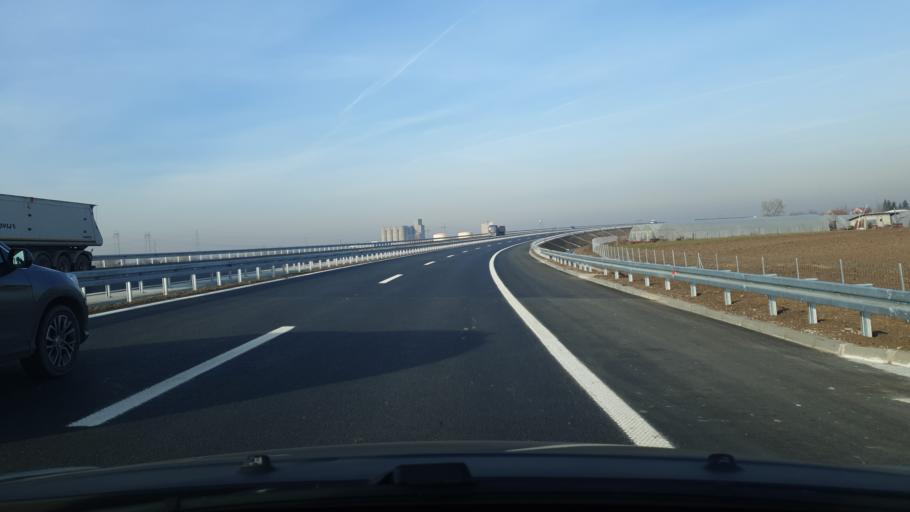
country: RS
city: Boljevci
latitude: 44.7604
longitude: 20.2459
